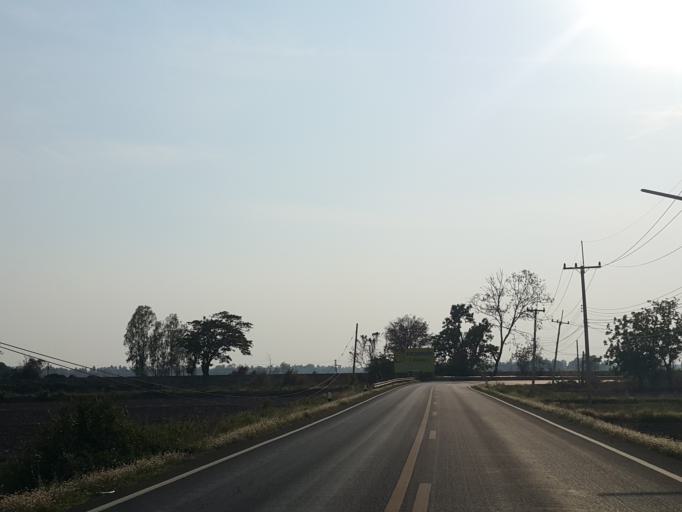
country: TH
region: Phitsanulok
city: Phrom Phiram
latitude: 17.1499
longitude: 100.1273
